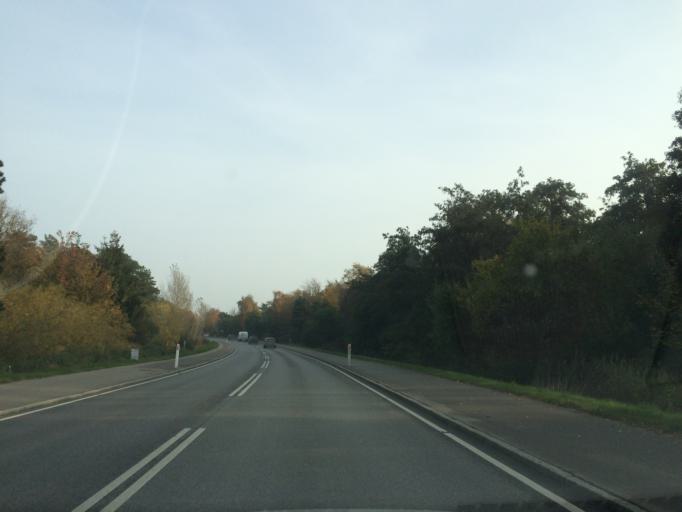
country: DK
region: Zealand
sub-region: Odsherred Kommune
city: Asnaes
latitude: 55.9783
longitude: 11.3246
